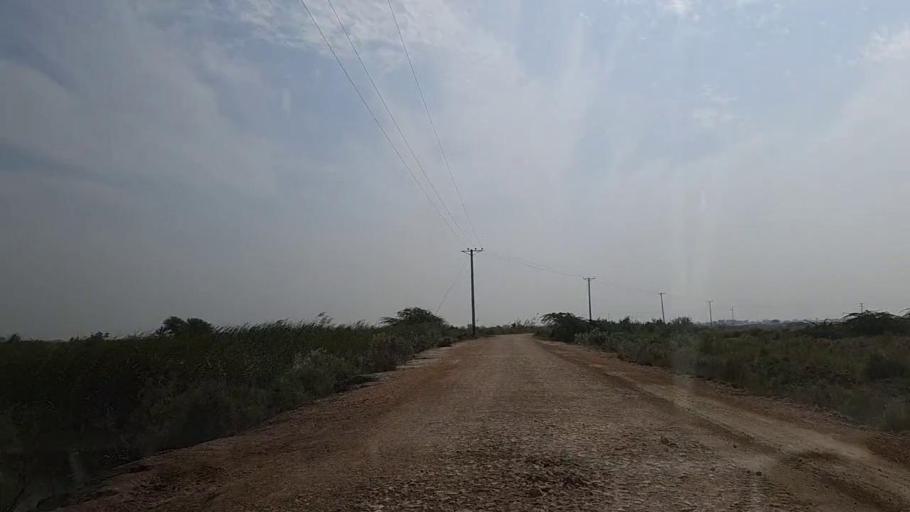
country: PK
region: Sindh
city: Mirpur Batoro
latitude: 24.6009
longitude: 68.2143
